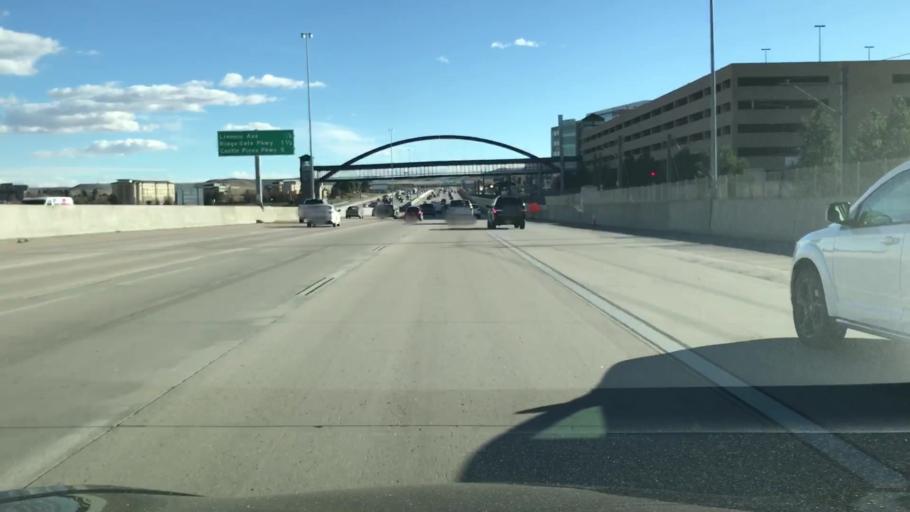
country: US
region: Colorado
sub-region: Douglas County
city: Meridian
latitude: 39.5488
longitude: -104.8691
